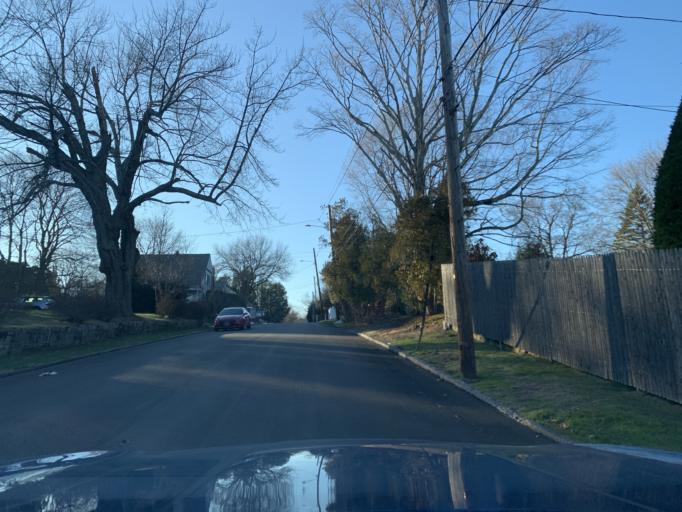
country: US
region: Rhode Island
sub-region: Kent County
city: West Warwick
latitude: 41.7122
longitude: -71.5304
